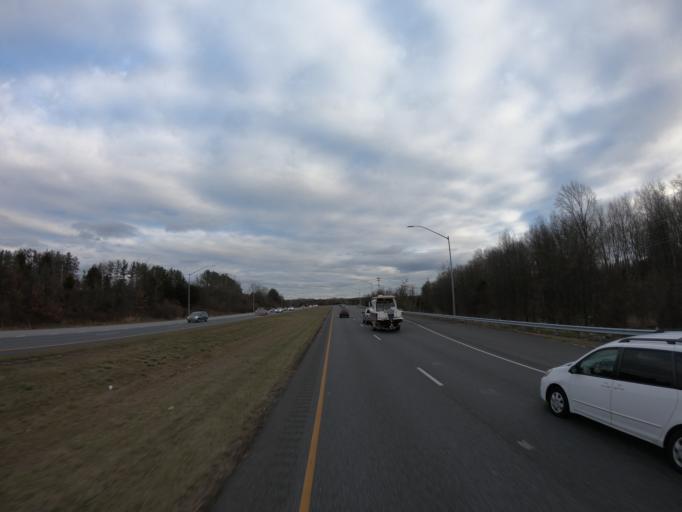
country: US
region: Maryland
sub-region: Howard County
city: Riverside
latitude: 39.1878
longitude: -76.9028
